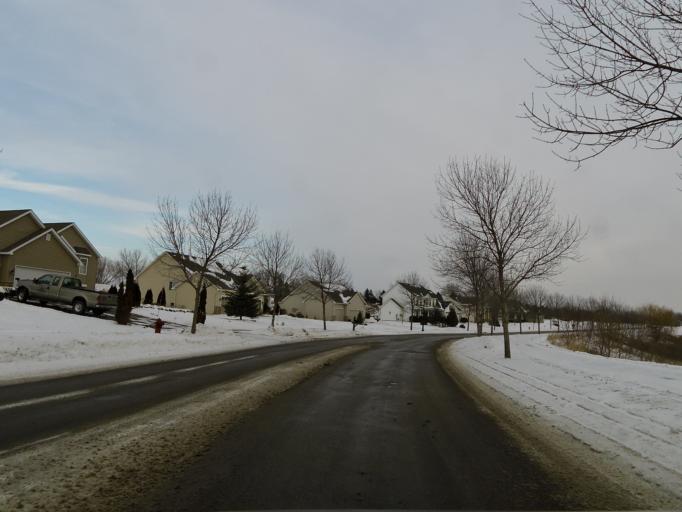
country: US
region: Minnesota
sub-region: Hennepin County
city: Saint Bonifacius
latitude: 44.9041
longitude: -93.7638
